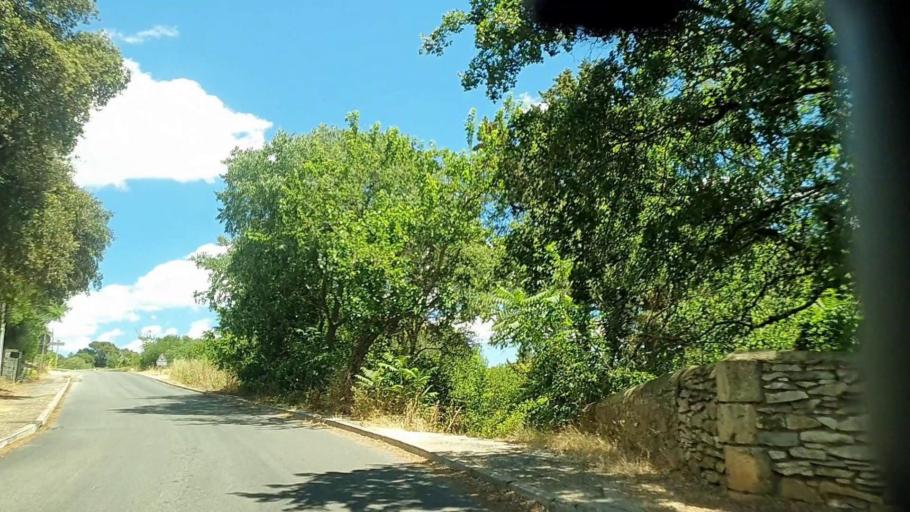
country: FR
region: Languedoc-Roussillon
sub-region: Departement du Gard
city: Cabrieres
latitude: 43.9059
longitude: 4.4727
